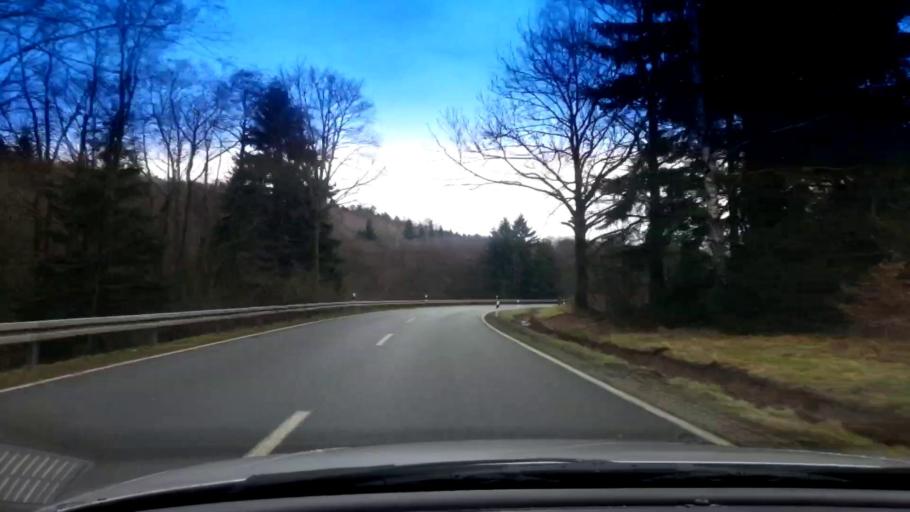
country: DE
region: Bavaria
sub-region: Upper Franconia
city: Gefrees
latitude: 50.0958
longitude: 11.7689
